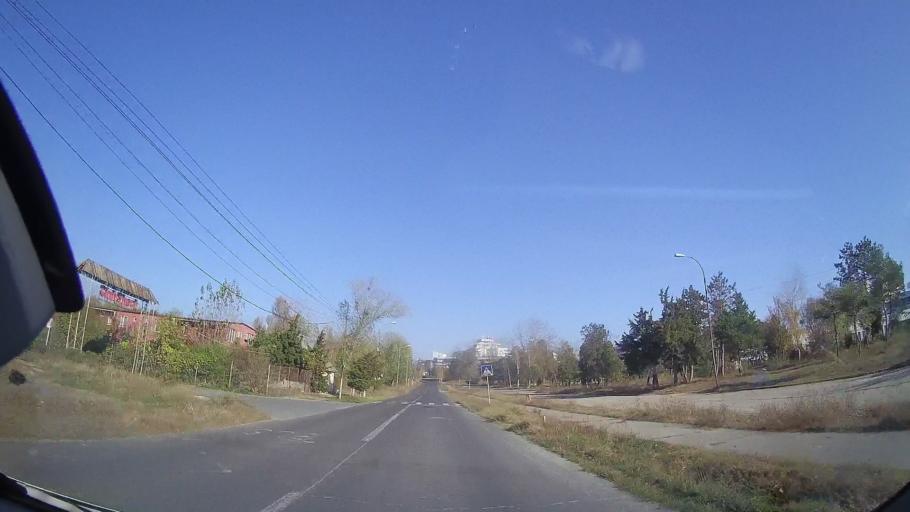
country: RO
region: Constanta
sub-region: Municipiul Mangalia
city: Mangalia
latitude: 43.8505
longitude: 28.6017
